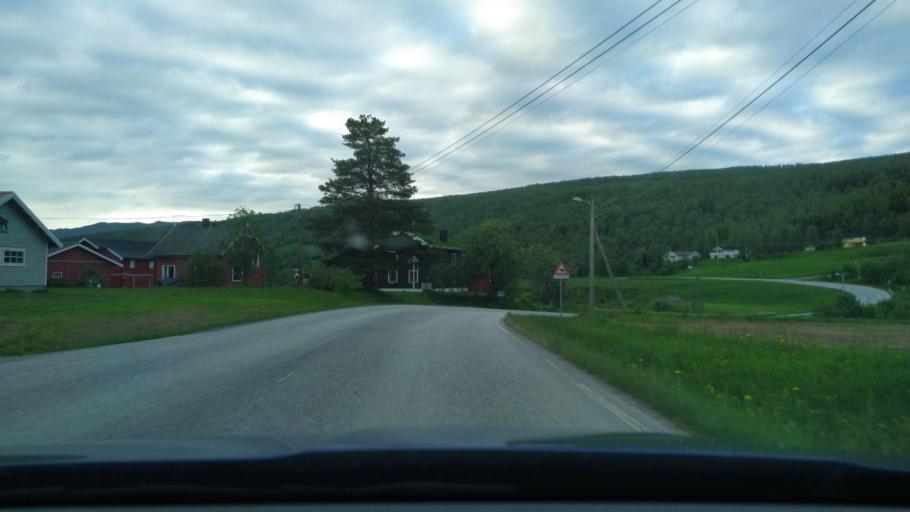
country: NO
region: Troms
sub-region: Sorreisa
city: Sorreisa
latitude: 69.1193
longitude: 18.2176
